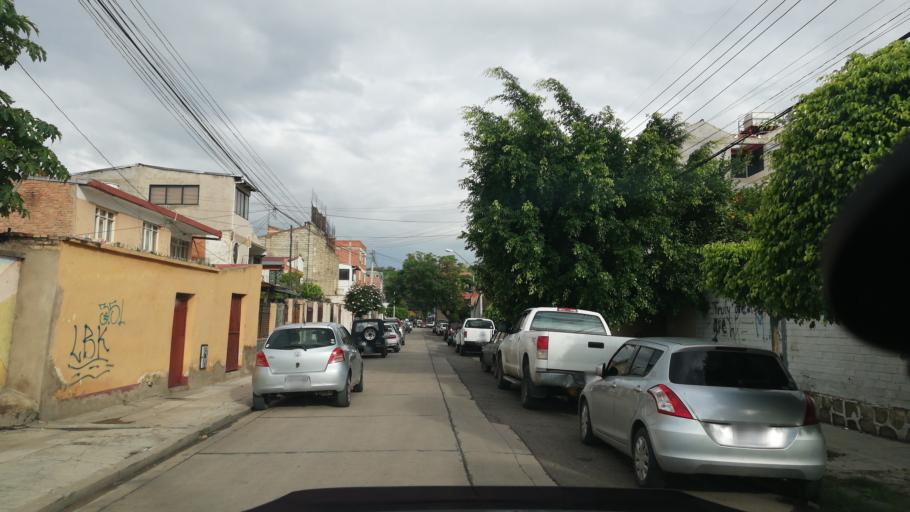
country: BO
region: Cochabamba
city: Cochabamba
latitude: -17.4017
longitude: -66.1655
